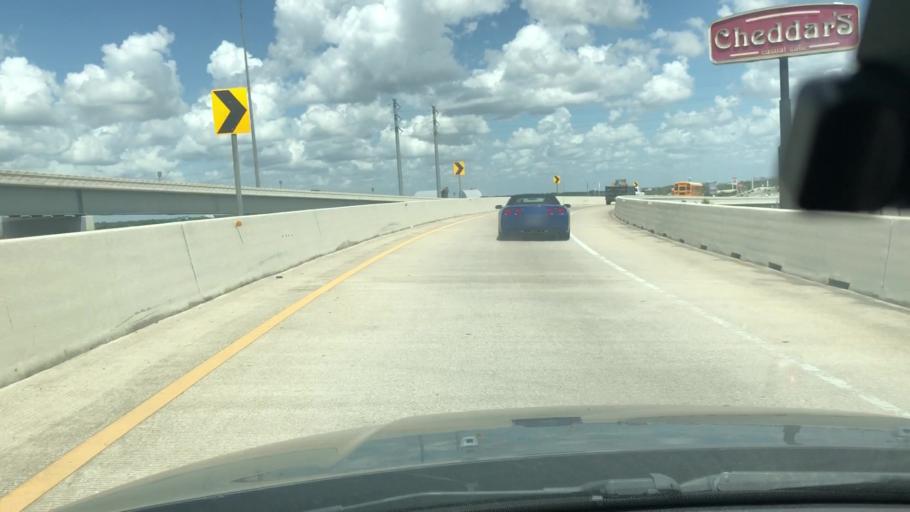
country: US
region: Texas
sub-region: Harris County
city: Webster
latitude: 29.5227
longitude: -95.1248
